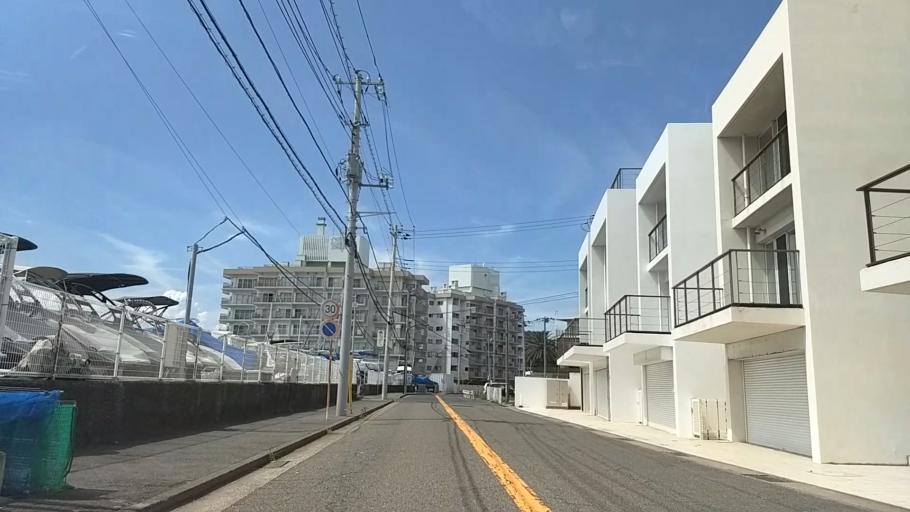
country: JP
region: Kanagawa
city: Hayama
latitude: 35.2279
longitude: 139.6038
